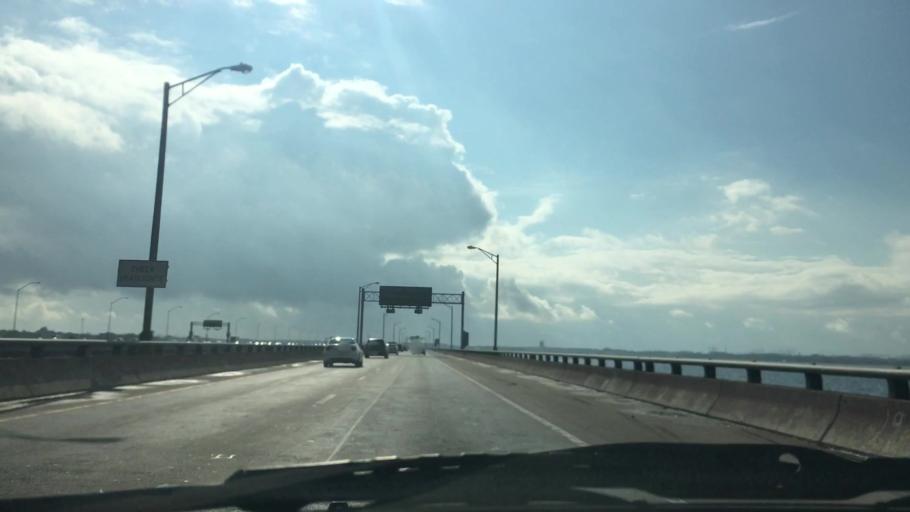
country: US
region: Virginia
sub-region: City of Hampton
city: East Hampton
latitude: 36.9783
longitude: -76.3011
